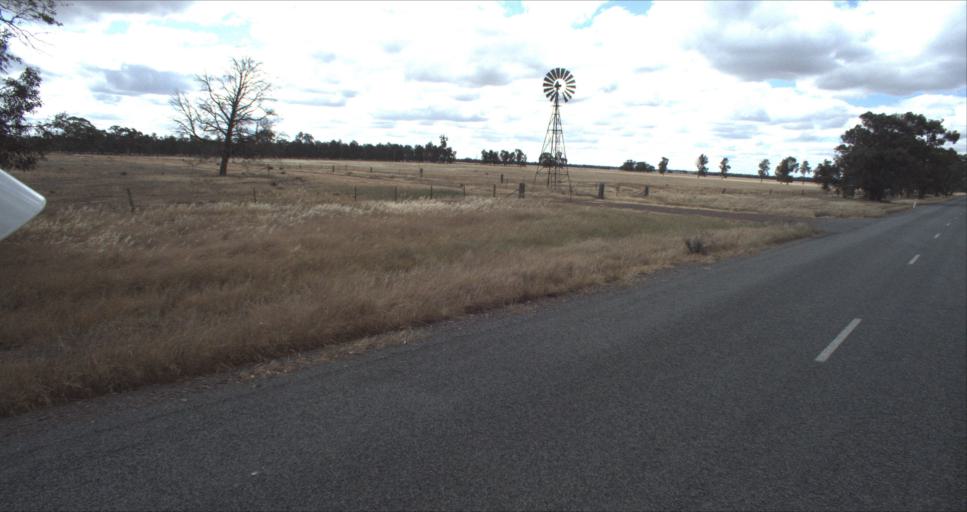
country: AU
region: New South Wales
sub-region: Leeton
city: Leeton
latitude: -34.6868
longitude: 146.3445
